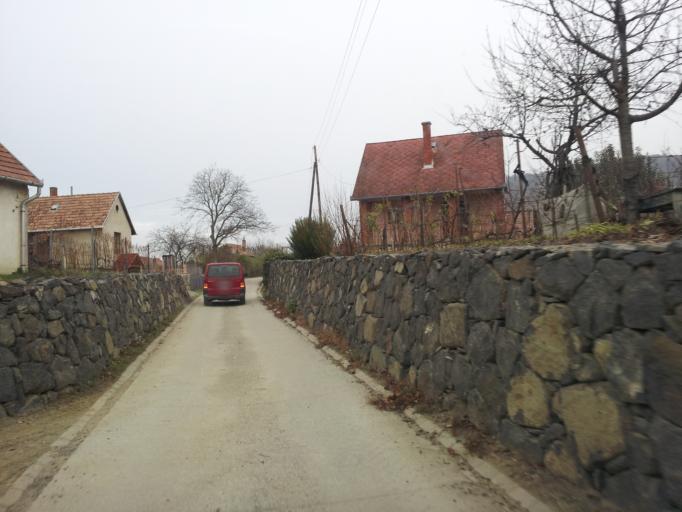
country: HU
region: Veszprem
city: Devecser
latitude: 47.1325
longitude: 17.3708
